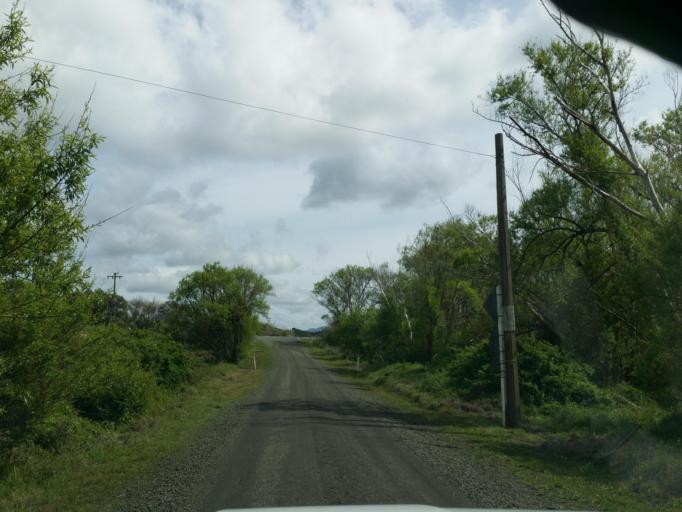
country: NZ
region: Northland
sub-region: Whangarei
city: Maungatapere
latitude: -35.8292
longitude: 174.0483
